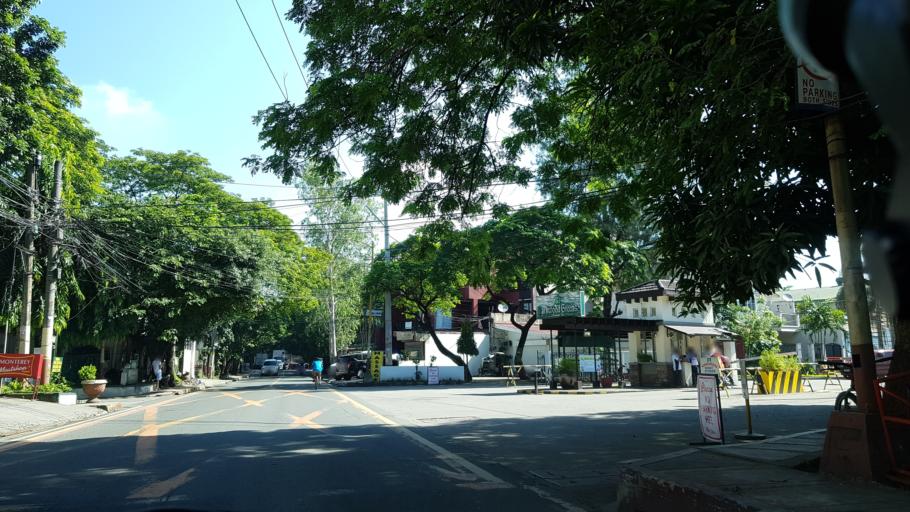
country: PH
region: Metro Manila
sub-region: Pasig
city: Pasig City
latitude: 14.5735
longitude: 121.0887
